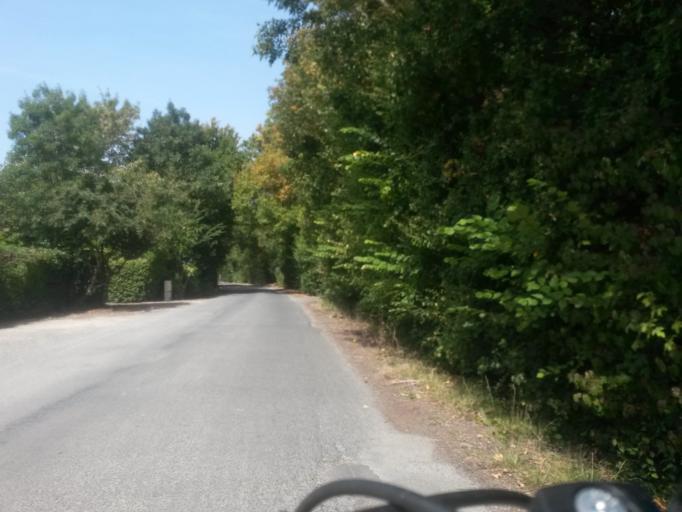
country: FR
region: Poitou-Charentes
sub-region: Departement de la Charente-Maritime
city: Saint-Xandre
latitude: 46.2138
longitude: -1.0941
